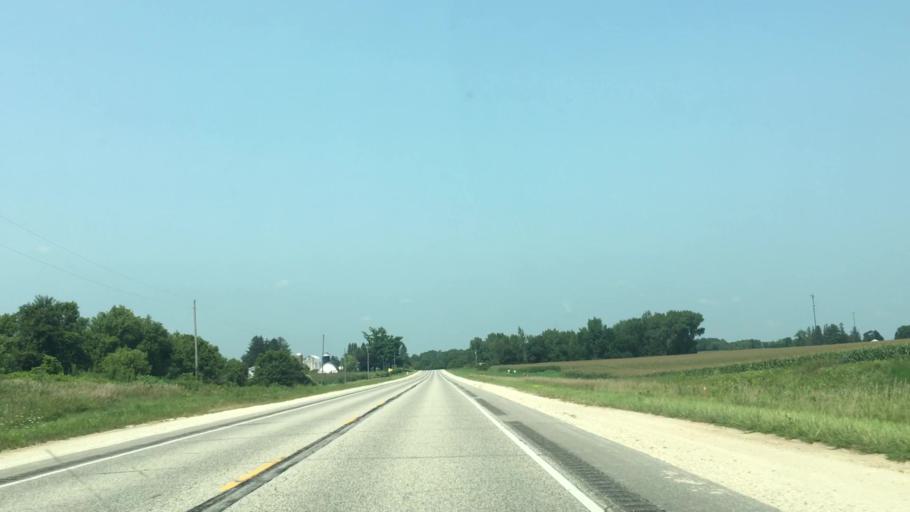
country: US
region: Iowa
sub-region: Fayette County
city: Fayette
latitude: 42.8218
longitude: -91.8050
